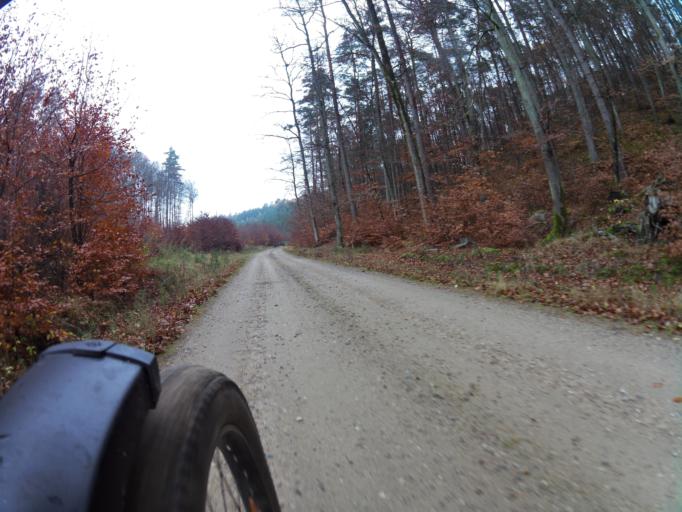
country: PL
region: Pomeranian Voivodeship
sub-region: Powiat wejherowski
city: Orle
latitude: 54.7066
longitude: 18.1461
